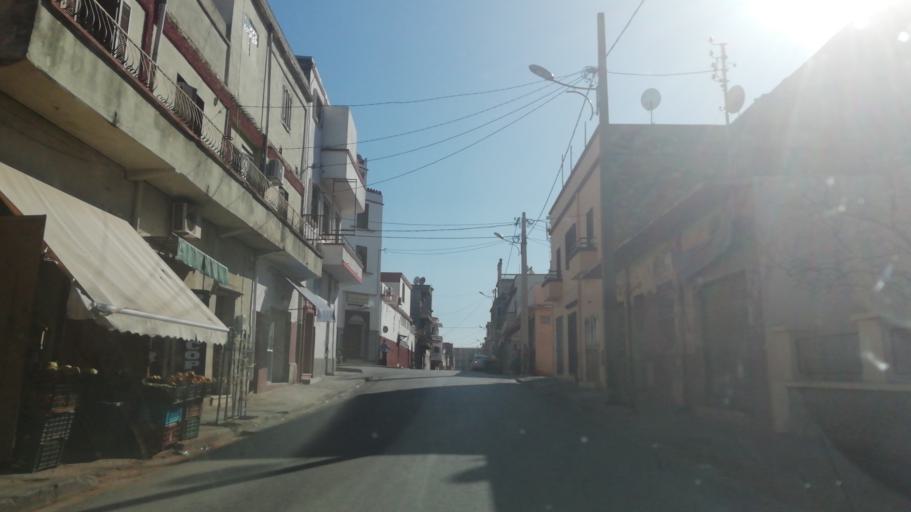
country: DZ
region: Oran
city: Oran
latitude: 35.7045
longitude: -0.6127
